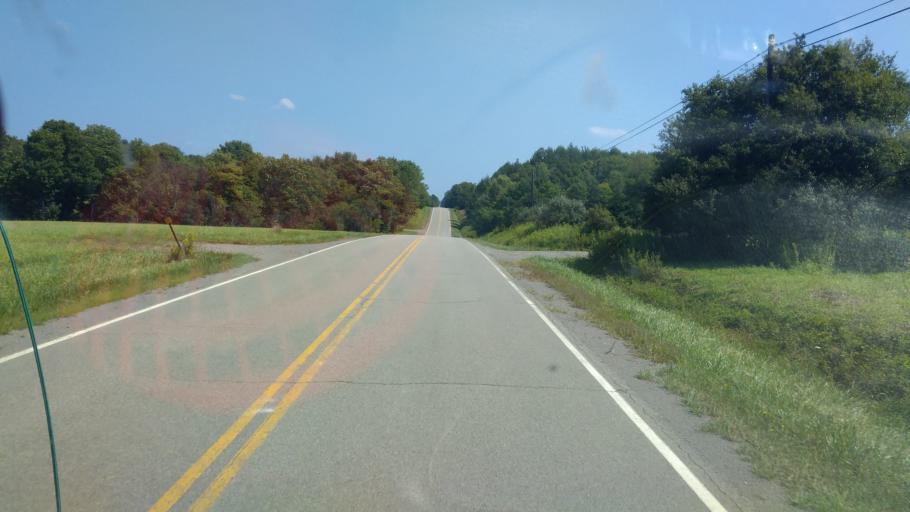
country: US
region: New York
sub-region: Allegany County
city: Belmont
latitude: 42.2920
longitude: -77.9232
